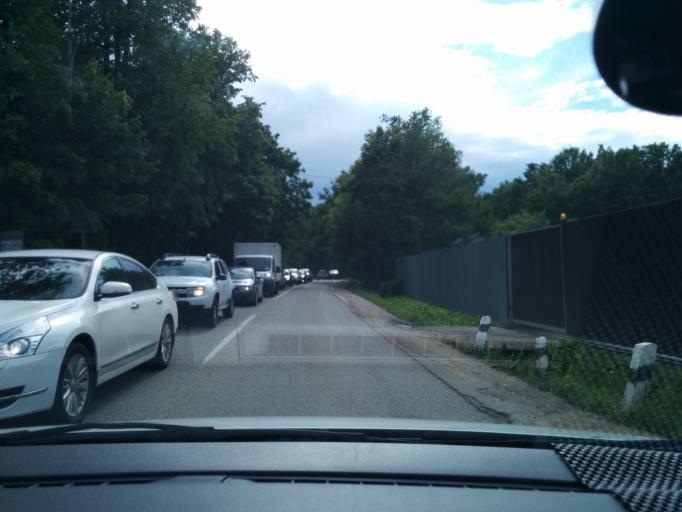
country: RU
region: Moskovskaya
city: Lugovaya
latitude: 56.0508
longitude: 37.4925
